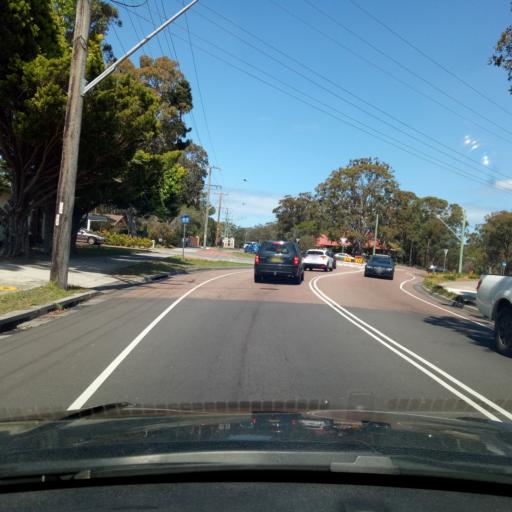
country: AU
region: New South Wales
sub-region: Wyong Shire
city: Tumbi Vmbi
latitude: -33.3687
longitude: 151.4498
